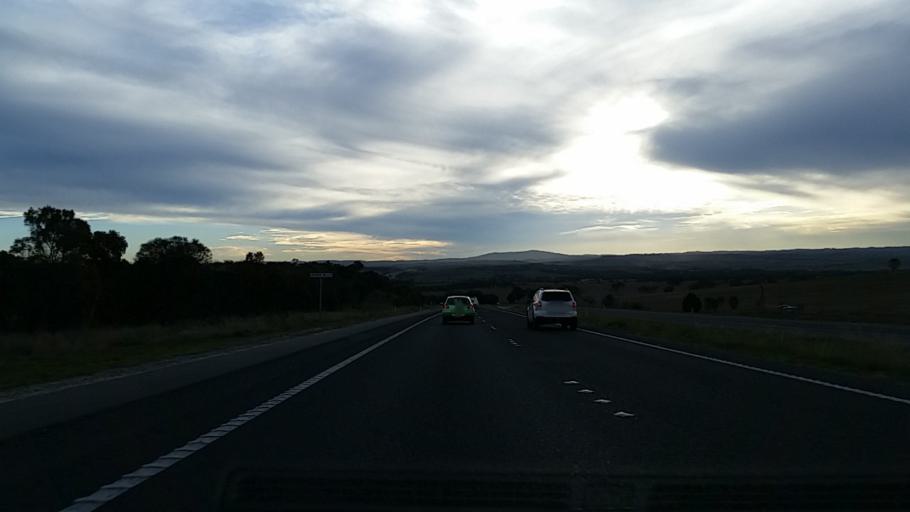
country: AU
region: South Australia
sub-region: Mount Barker
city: Callington
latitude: -35.1343
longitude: 139.0651
